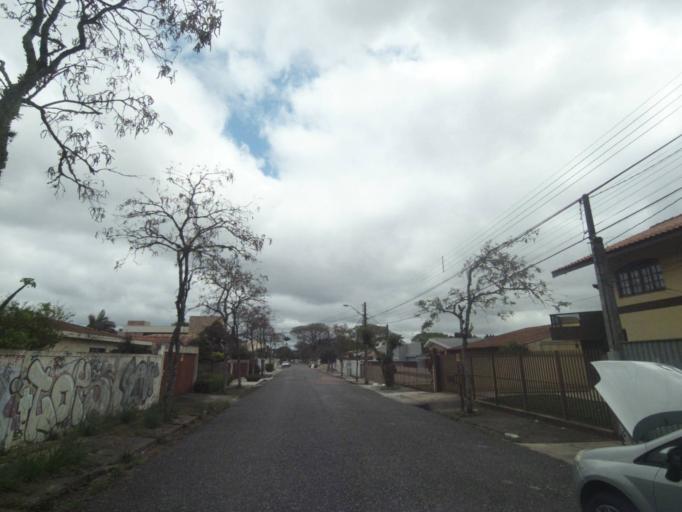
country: BR
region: Parana
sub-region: Pinhais
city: Pinhais
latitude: -25.3988
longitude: -49.2214
